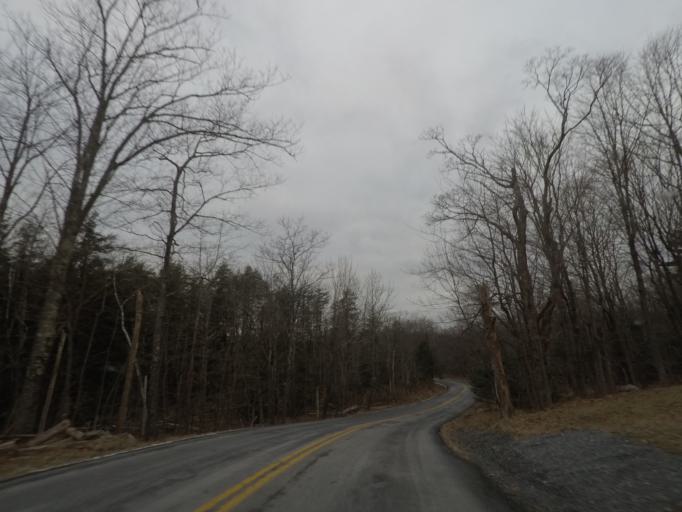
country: US
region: New York
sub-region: Rensselaer County
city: Poestenkill
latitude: 42.7326
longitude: -73.5060
